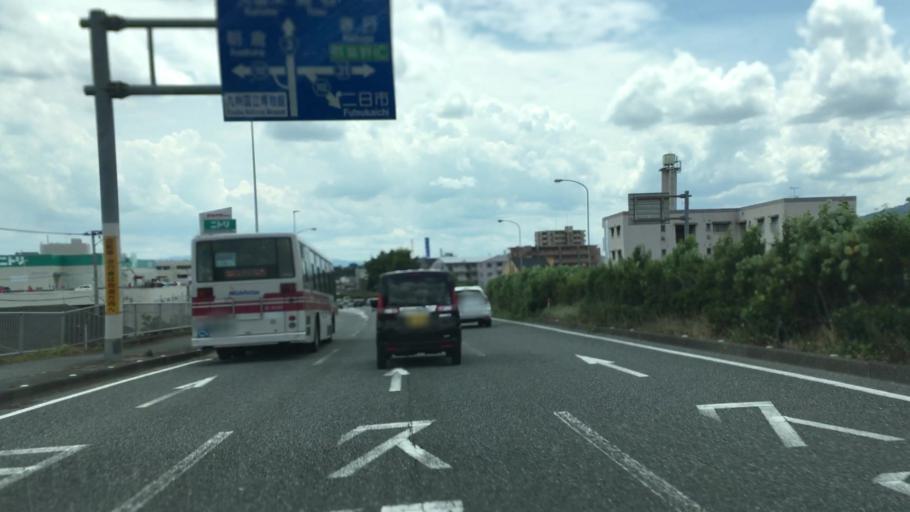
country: JP
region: Fukuoka
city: Chikushino-shi
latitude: 33.4879
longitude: 130.5358
